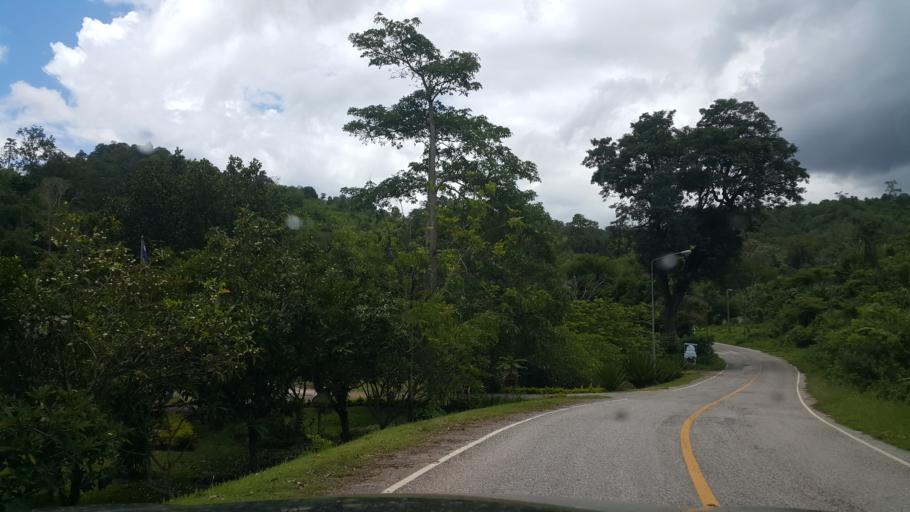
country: TH
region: Loei
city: Na Haeo
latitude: 17.6293
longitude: 100.8947
